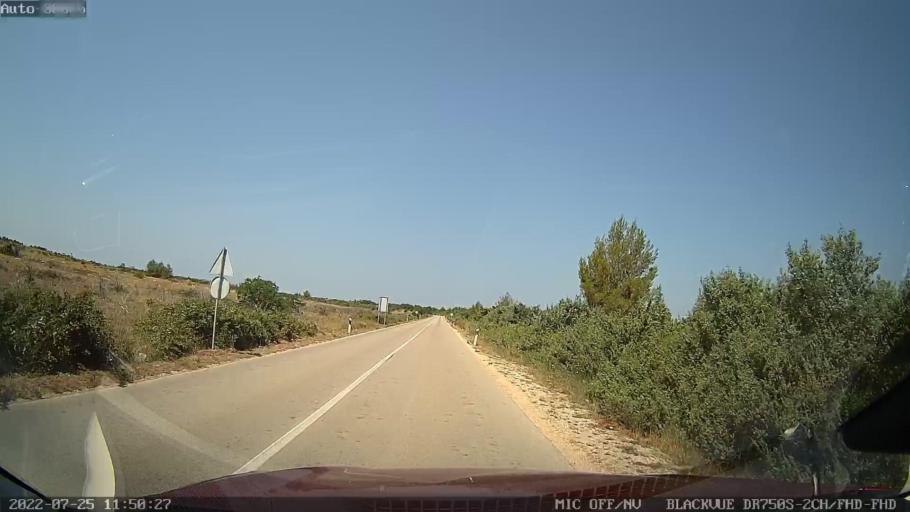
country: HR
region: Zadarska
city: Vrsi
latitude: 44.2367
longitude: 15.2655
